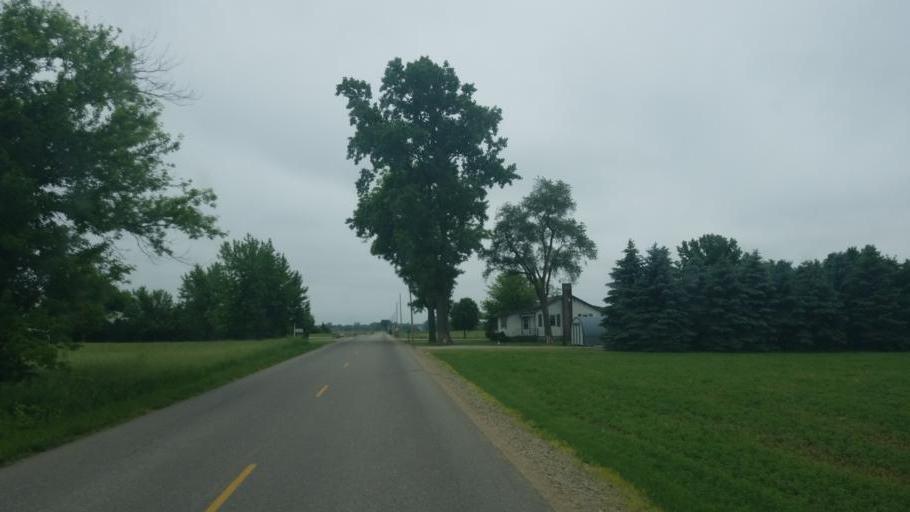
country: US
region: Indiana
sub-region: Elkhart County
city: Nappanee
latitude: 41.4656
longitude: -86.0208
